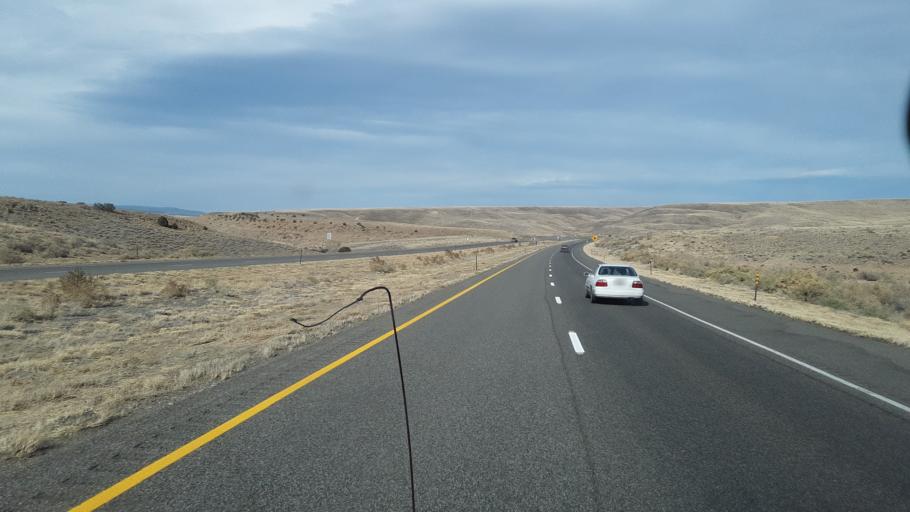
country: US
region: Colorado
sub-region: Delta County
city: Delta
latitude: 38.8053
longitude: -108.2752
